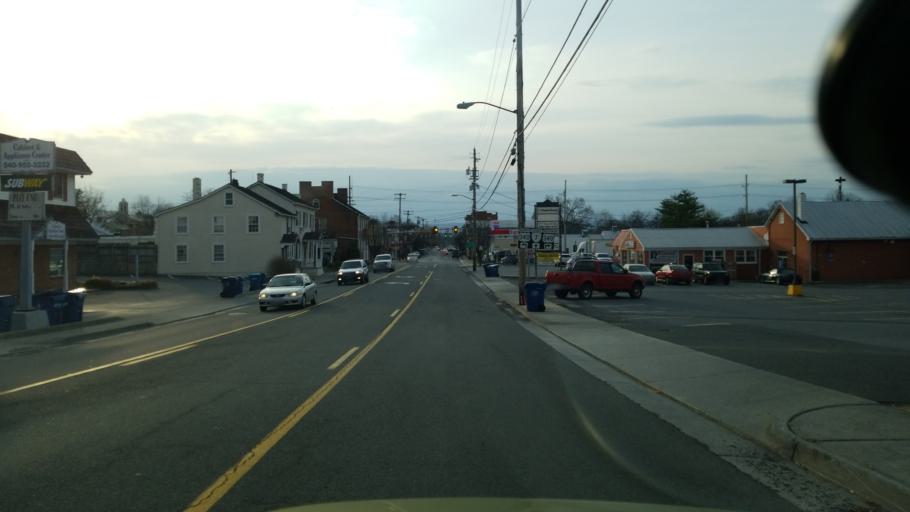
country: US
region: Virginia
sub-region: Clarke County
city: Berryville
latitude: 39.1524
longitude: -77.9839
